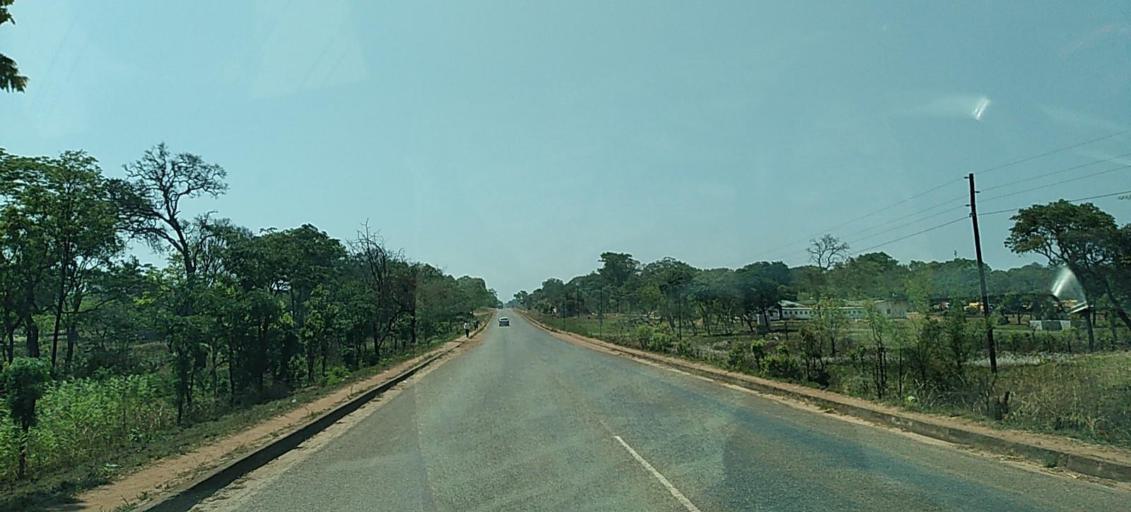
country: ZM
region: North-Western
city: Solwezi
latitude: -12.3355
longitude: 25.8977
